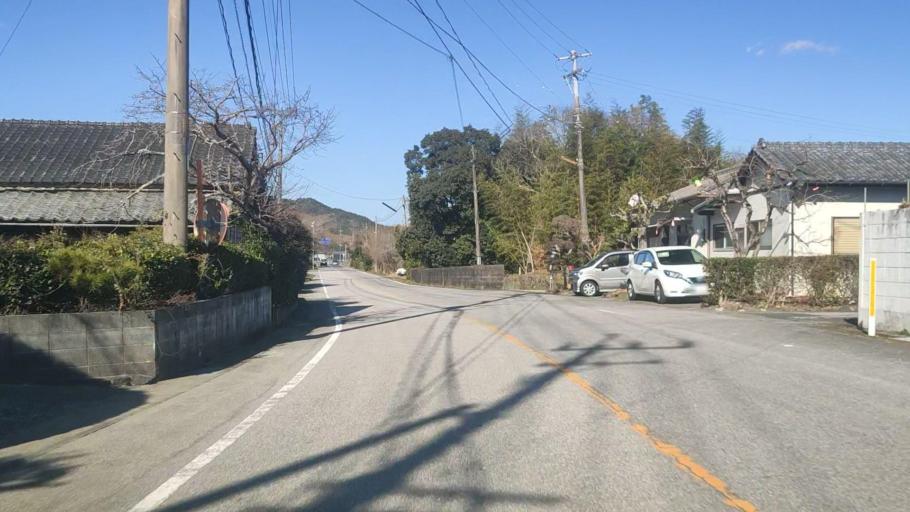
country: JP
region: Oita
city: Saiki
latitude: 32.9059
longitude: 131.9320
